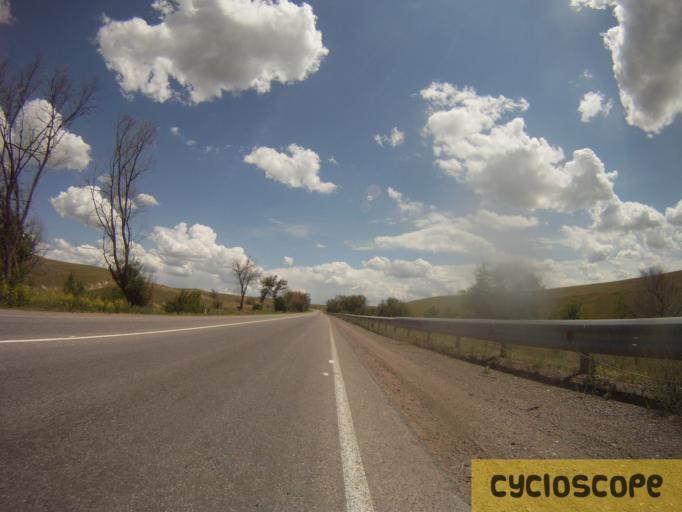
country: KZ
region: Almaty Oblysy
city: Burunday
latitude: 43.3119
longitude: 76.1776
